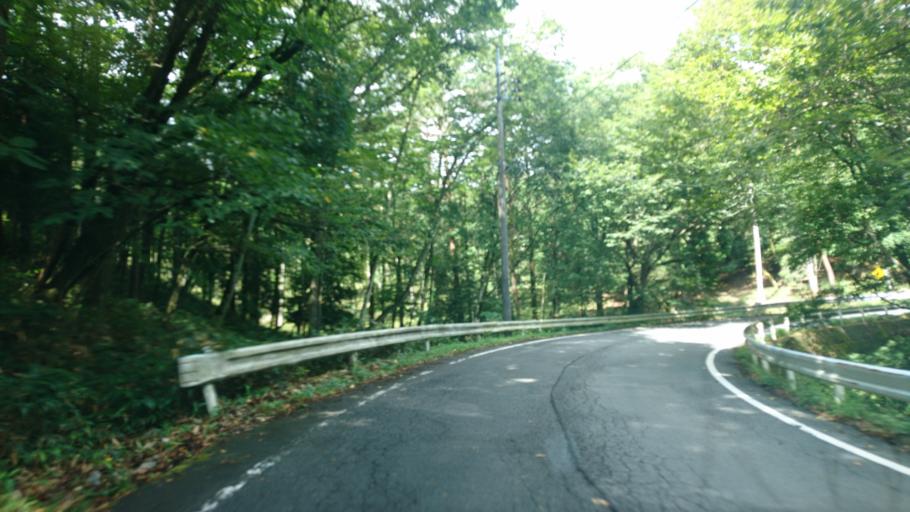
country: JP
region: Gunma
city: Omamacho-omama
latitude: 36.5803
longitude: 139.2339
